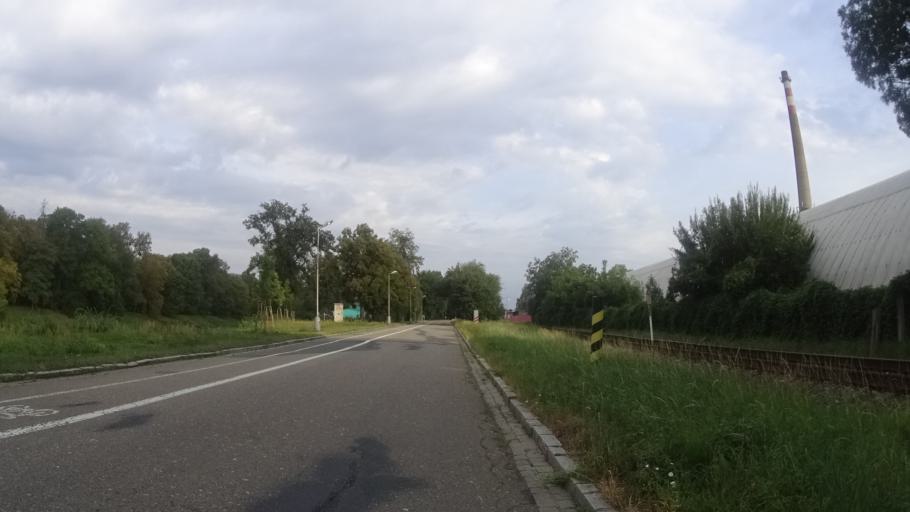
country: CZ
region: Zlin
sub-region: Okres Kromeriz
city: Kromeriz
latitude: 49.3059
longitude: 17.3969
